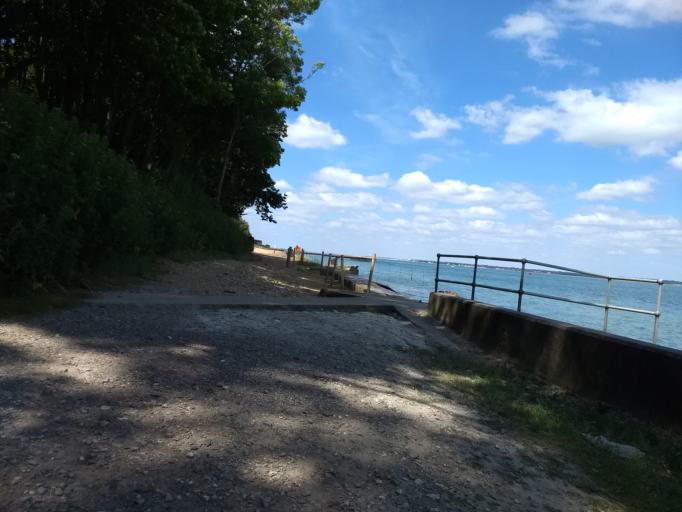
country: GB
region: England
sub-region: Isle of Wight
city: Yarmouth
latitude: 50.7069
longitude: -1.5155
